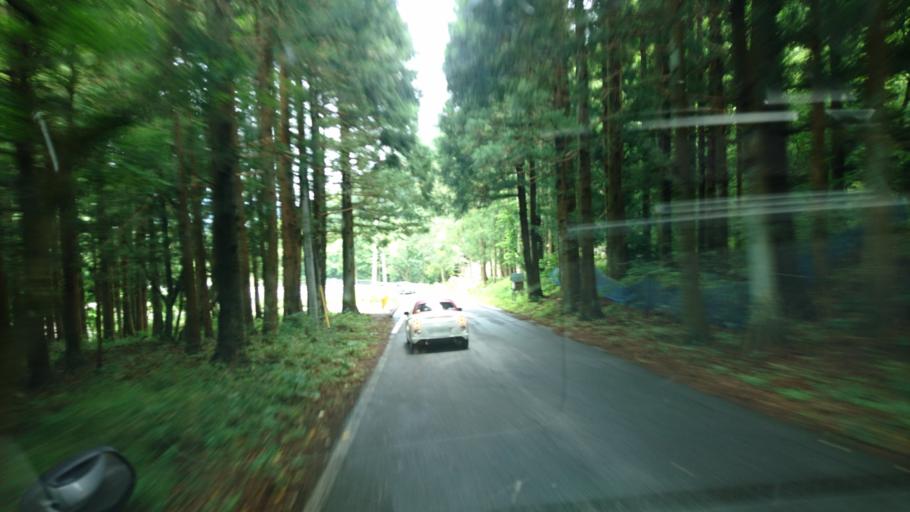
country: JP
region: Iwate
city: Ofunato
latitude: 39.1320
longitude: 141.7934
